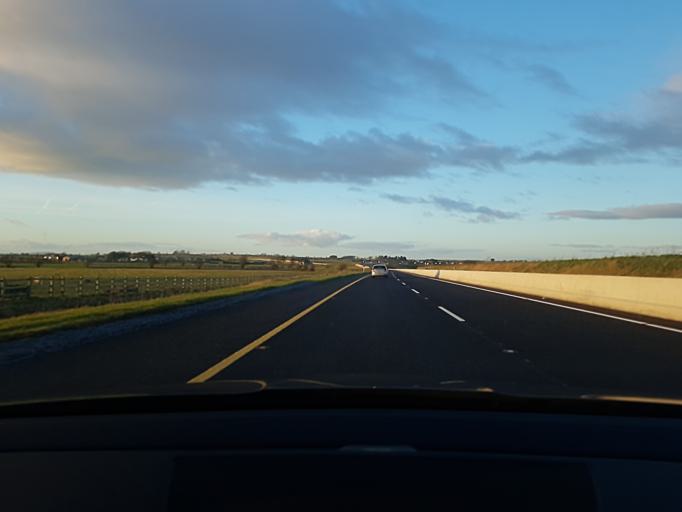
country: IE
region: Connaught
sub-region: County Galway
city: Athenry
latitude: 53.3857
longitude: -8.8008
